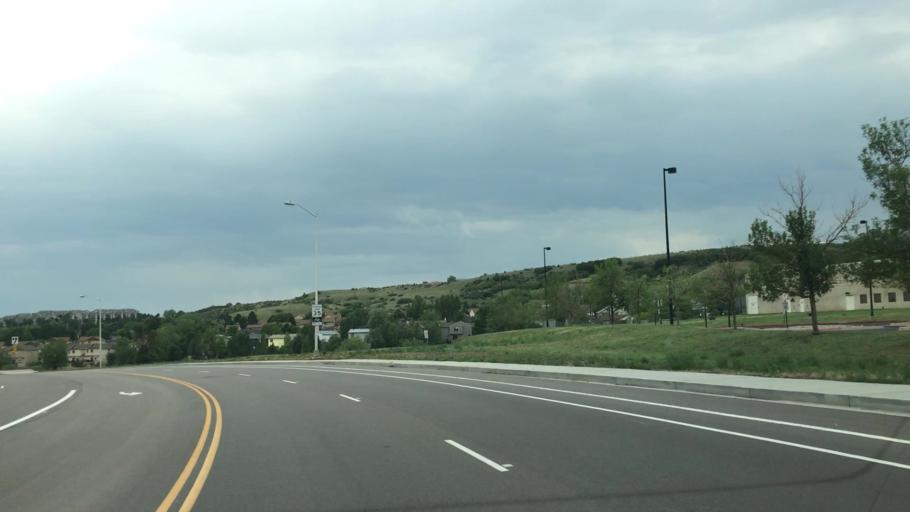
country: US
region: Colorado
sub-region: El Paso County
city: Colorado Springs
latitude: 38.8939
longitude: -104.8517
